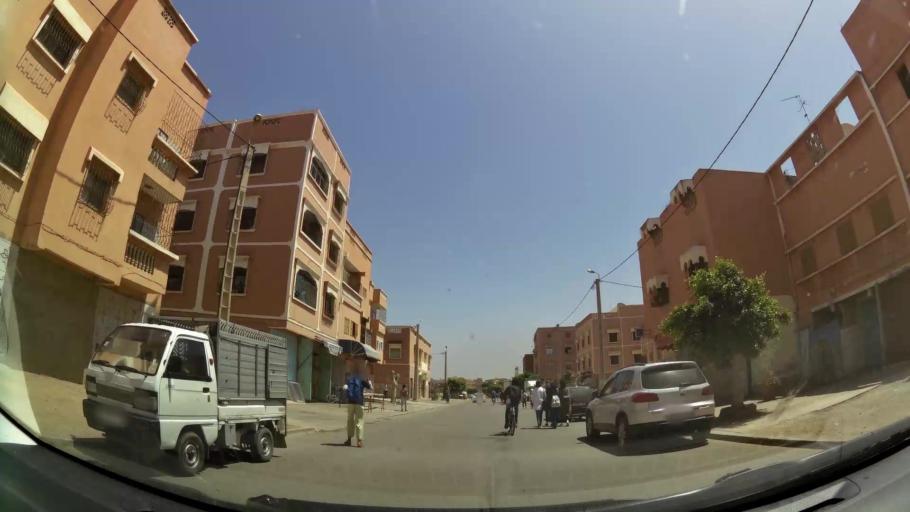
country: MA
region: Souss-Massa-Draa
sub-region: Inezgane-Ait Mellou
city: Inezgane
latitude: 30.3480
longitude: -9.4896
